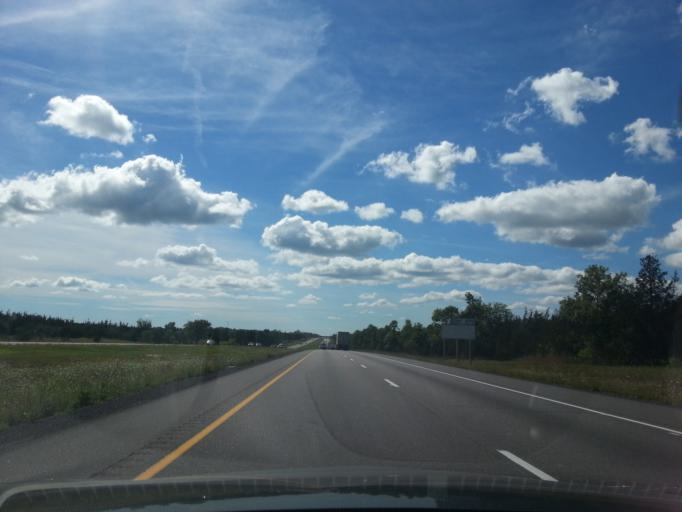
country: CA
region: Ontario
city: Deseronto
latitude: 44.2473
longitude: -77.0437
